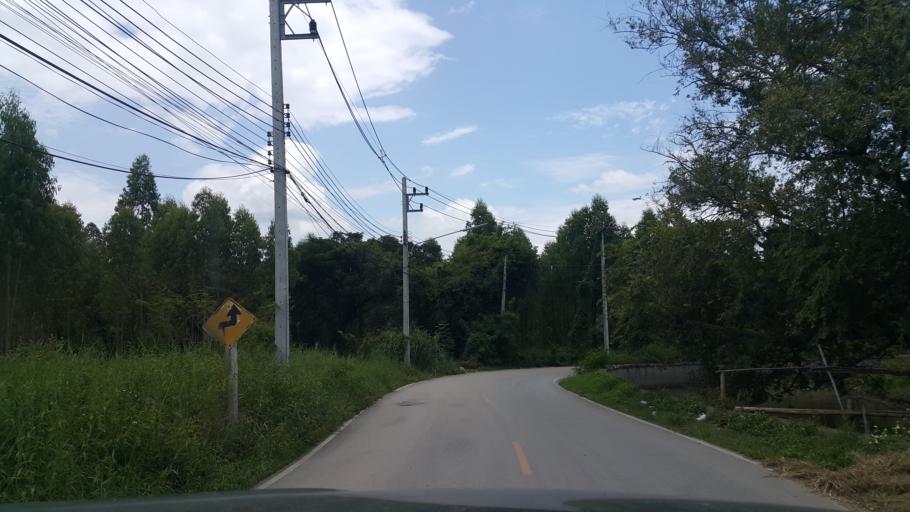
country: TH
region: Chiang Mai
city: Saraphi
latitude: 18.7137
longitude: 98.9788
